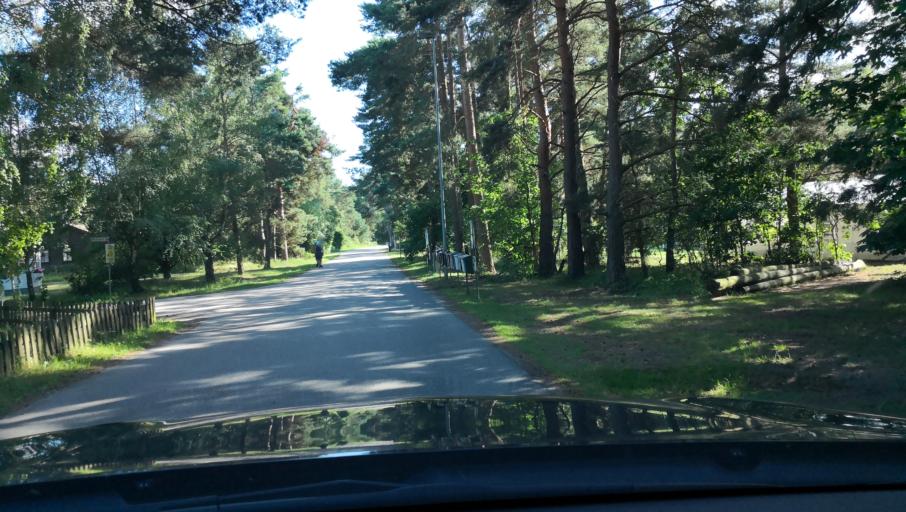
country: SE
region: Skane
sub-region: Simrishamns Kommun
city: Kivik
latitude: 55.7836
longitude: 14.1950
